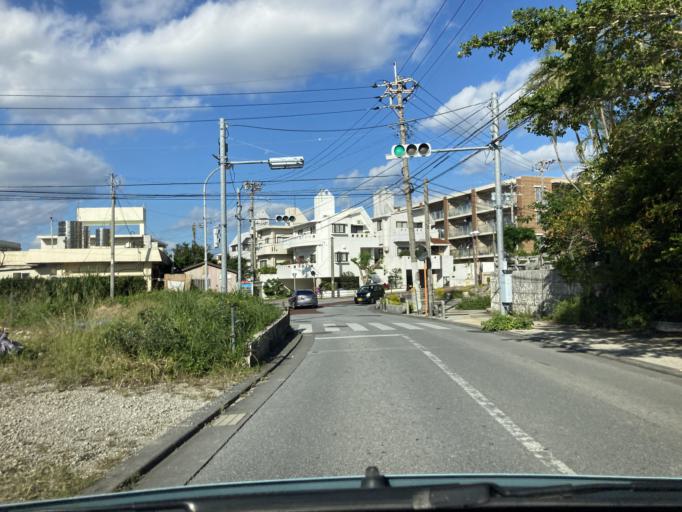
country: JP
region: Okinawa
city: Ginowan
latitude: 26.2246
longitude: 127.7325
